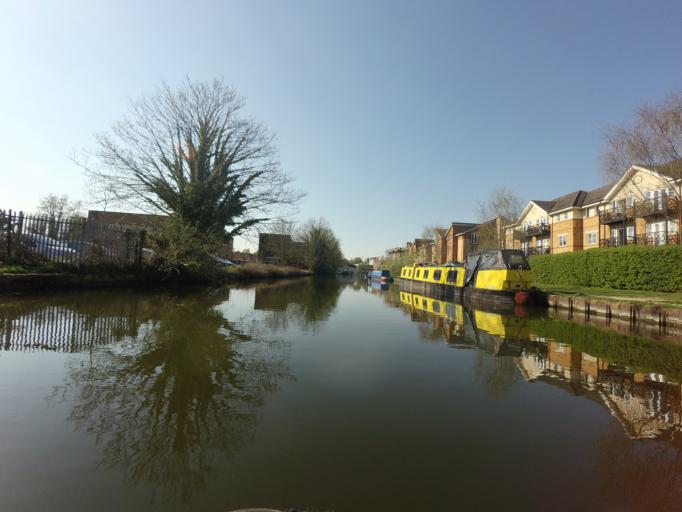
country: GB
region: England
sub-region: Hertfordshire
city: Hemel Hempstead
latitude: 51.7368
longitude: -0.4643
